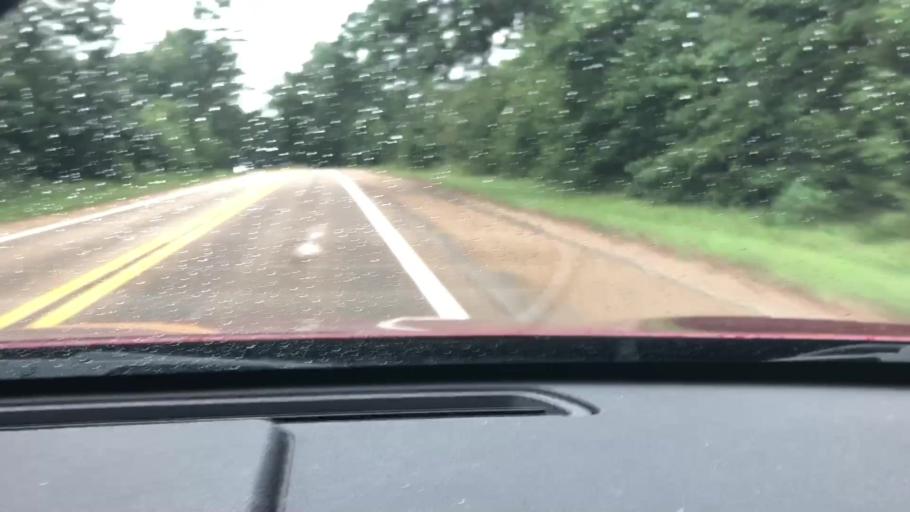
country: US
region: Arkansas
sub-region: Lafayette County
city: Stamps
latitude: 33.3568
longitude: -93.4039
